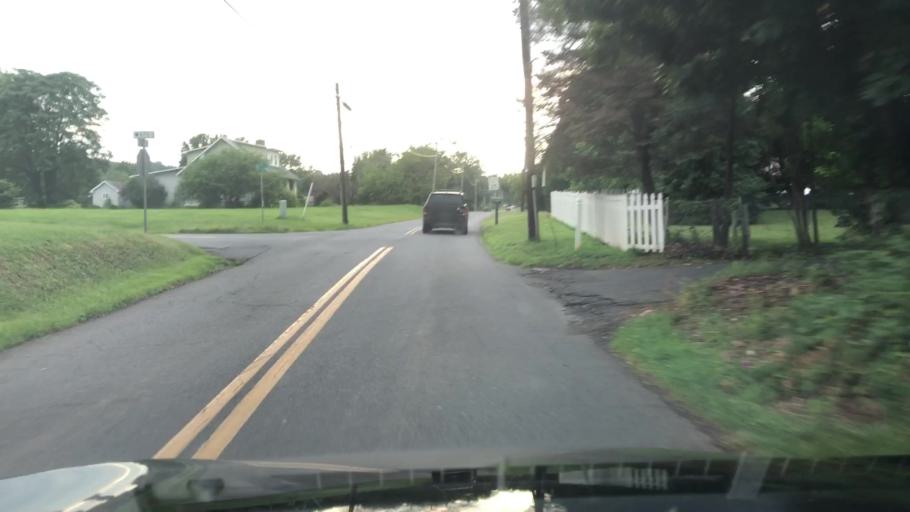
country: US
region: Virginia
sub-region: Fauquier County
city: New Baltimore
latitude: 38.7639
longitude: -77.7124
